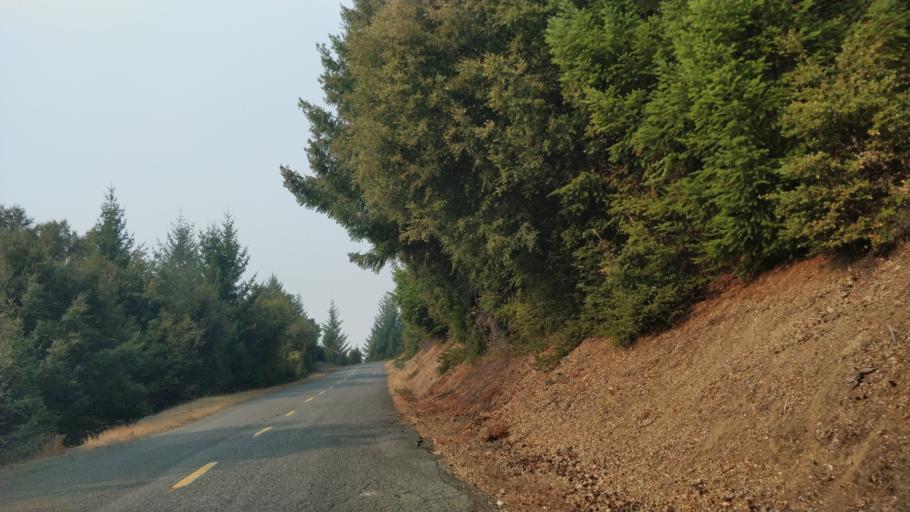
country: US
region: California
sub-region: Humboldt County
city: Rio Dell
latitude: 40.2551
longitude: -124.1173
